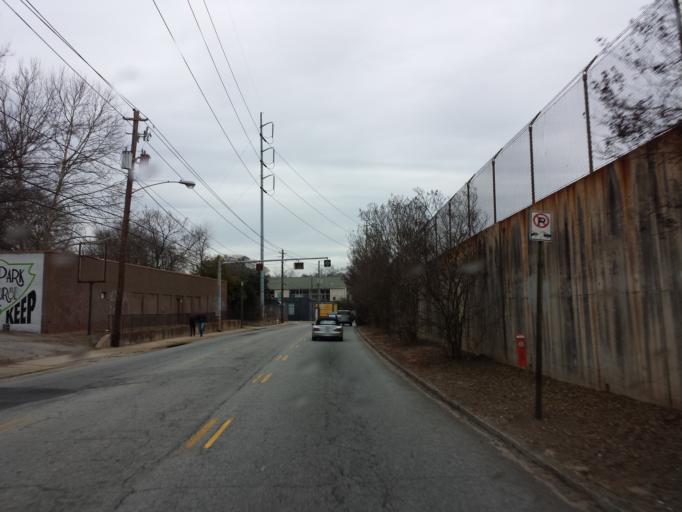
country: US
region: Georgia
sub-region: DeKalb County
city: Druid Hills
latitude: 33.7626
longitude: -84.3363
